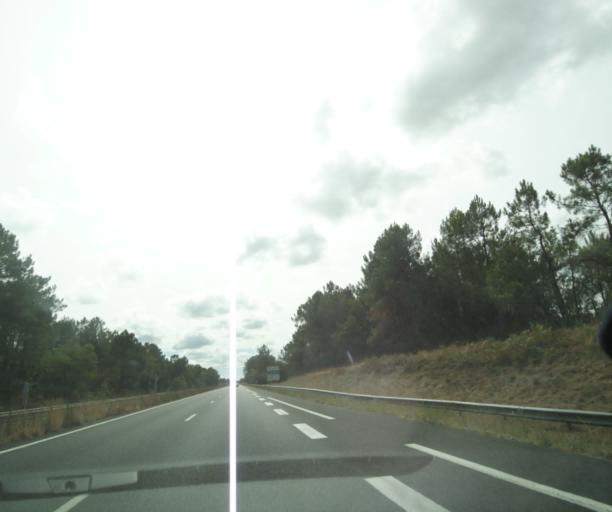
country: FR
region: Aquitaine
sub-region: Departement de la Gironde
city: Marcillac
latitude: 45.2503
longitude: -0.5394
